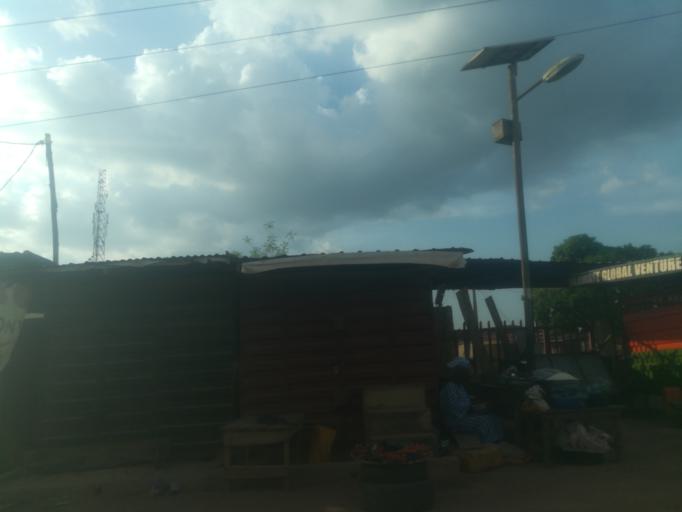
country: NG
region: Ogun
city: Abeokuta
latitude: 7.1200
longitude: 3.3197
